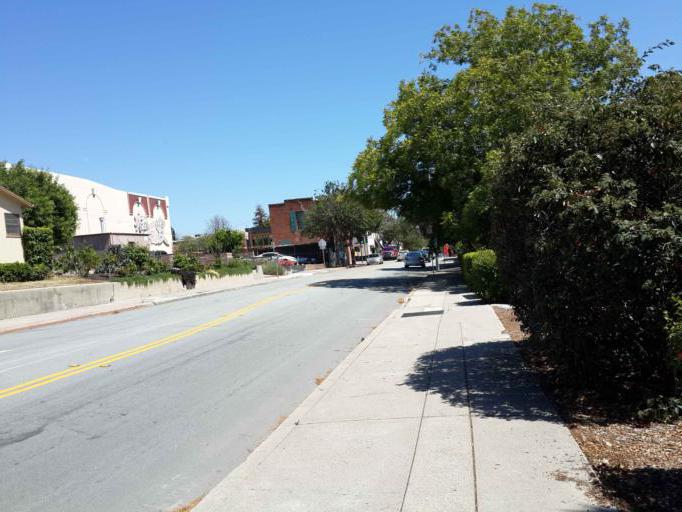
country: US
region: California
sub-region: San Luis Obispo County
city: San Luis Obispo
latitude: 35.2822
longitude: -120.6650
